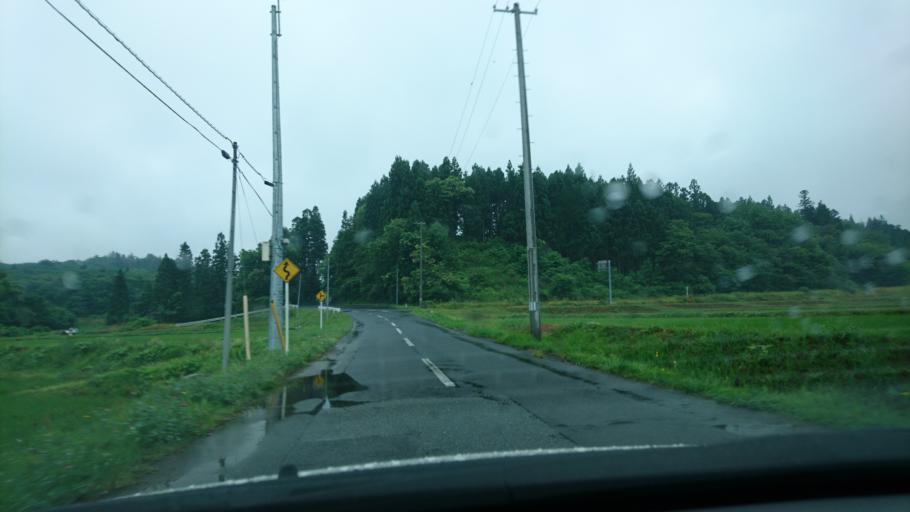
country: JP
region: Iwate
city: Ichinoseki
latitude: 38.8944
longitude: 141.0342
